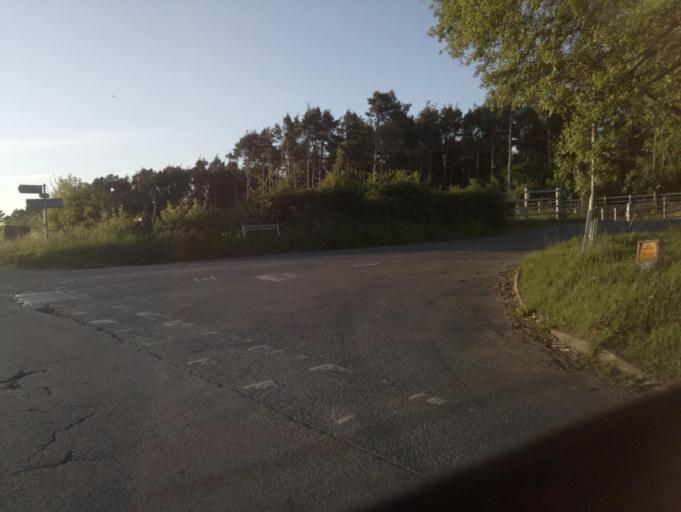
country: GB
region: England
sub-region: Devon
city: Newton Abbot
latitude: 50.5477
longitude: -3.6344
